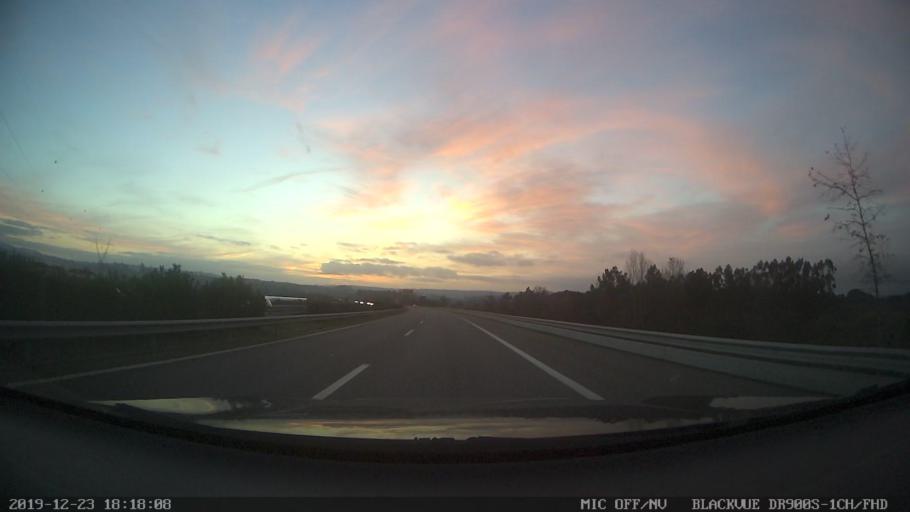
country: PT
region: Coimbra
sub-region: Condeixa-A-Nova
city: Condeixa-a-Nova
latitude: 40.1256
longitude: -8.5087
